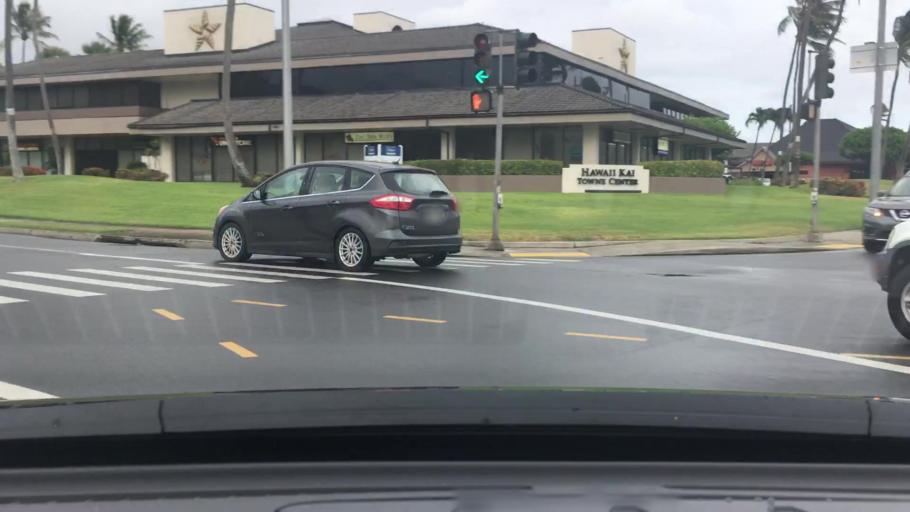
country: US
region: Hawaii
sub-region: Honolulu County
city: Waimanalo Beach
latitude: 21.2832
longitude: -157.7153
